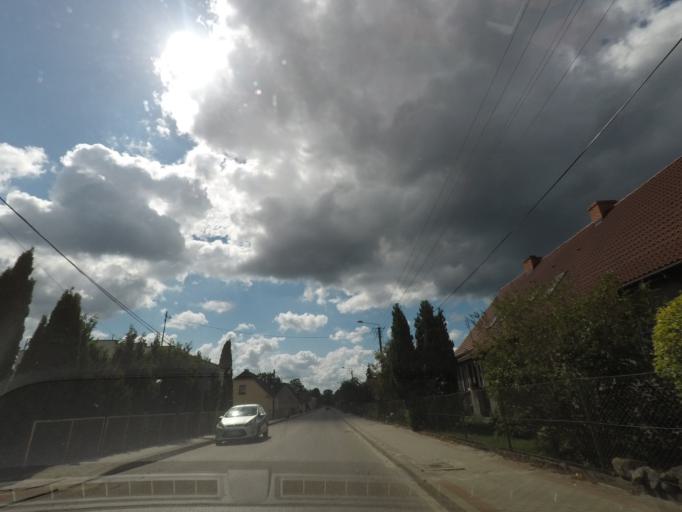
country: PL
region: Pomeranian Voivodeship
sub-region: Powiat wejherowski
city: Leczyce
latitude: 54.5936
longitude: 17.8607
